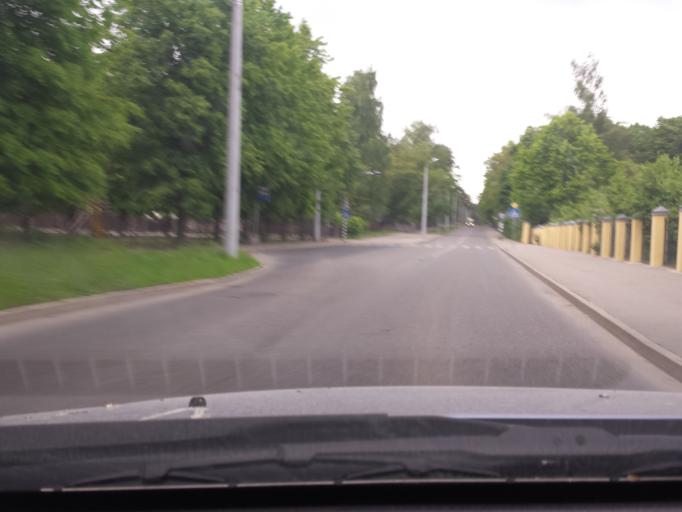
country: LV
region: Riga
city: Jaunciems
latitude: 57.0034
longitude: 24.1690
